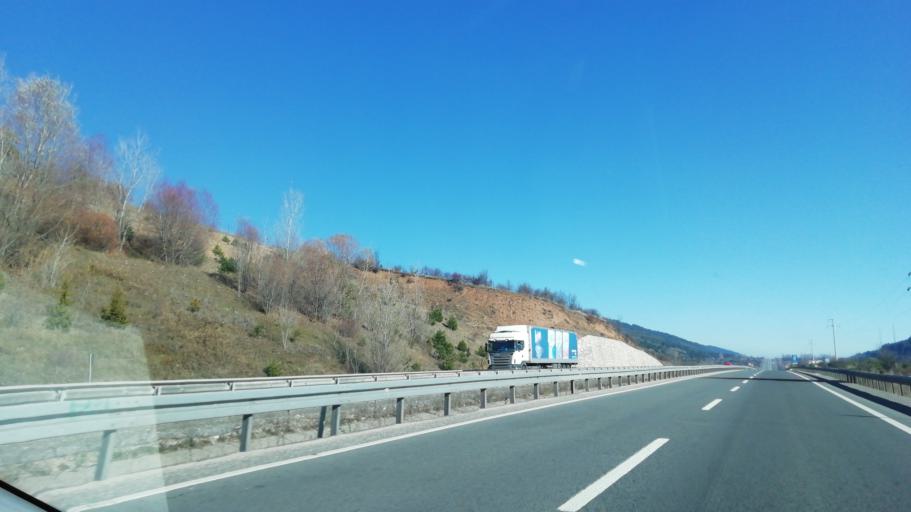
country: TR
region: Bolu
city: Gerede
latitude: 40.8104
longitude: 32.2604
